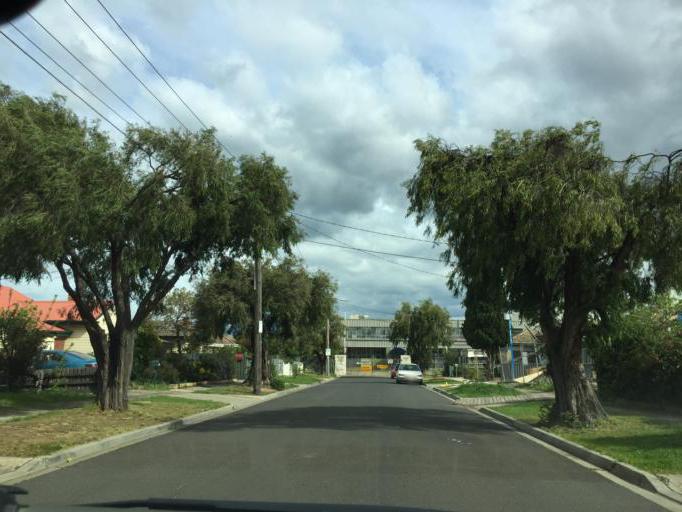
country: AU
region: Victoria
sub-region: Maribyrnong
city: Braybrook
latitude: -37.8021
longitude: 144.8608
